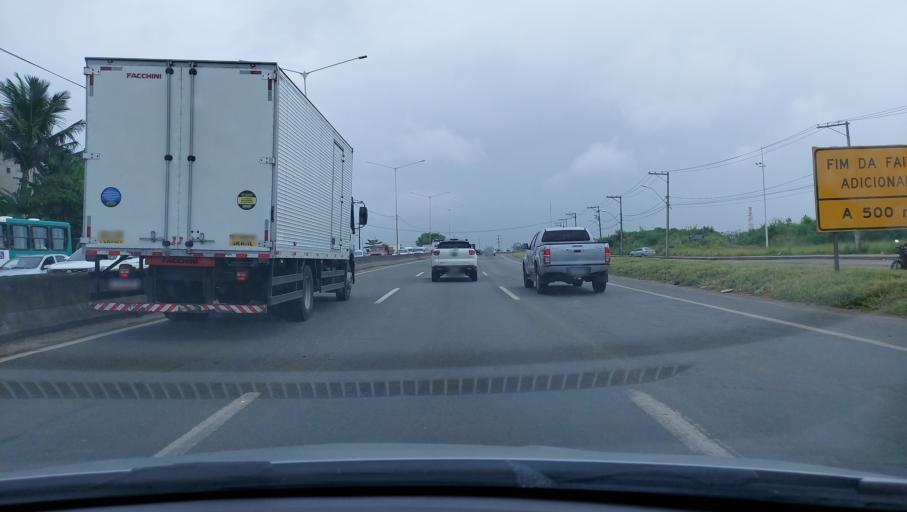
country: BR
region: Bahia
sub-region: Salvador
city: Salvador
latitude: -12.8921
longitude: -38.4460
